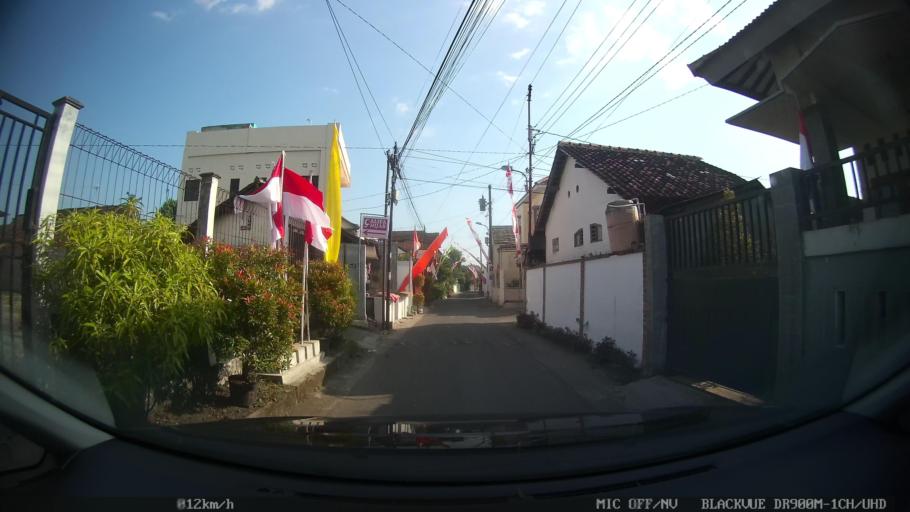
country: ID
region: Daerah Istimewa Yogyakarta
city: Yogyakarta
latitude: -7.7987
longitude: 110.3490
